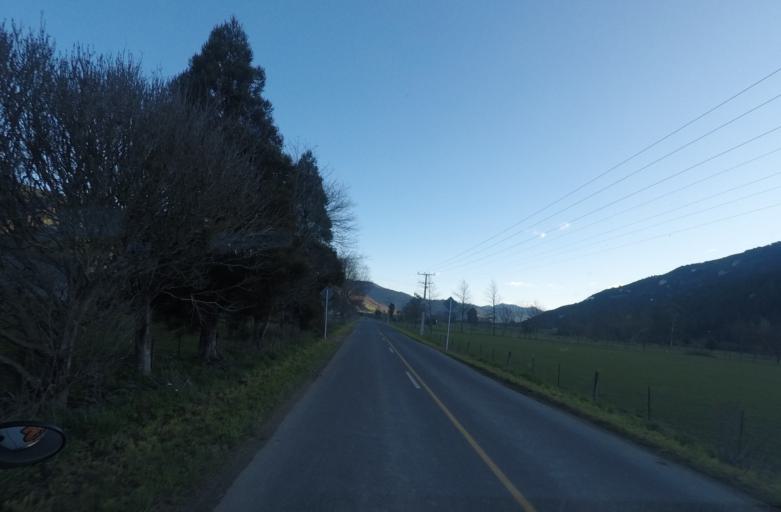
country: NZ
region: Marlborough
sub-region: Marlborough District
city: Picton
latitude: -41.2834
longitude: 173.9112
